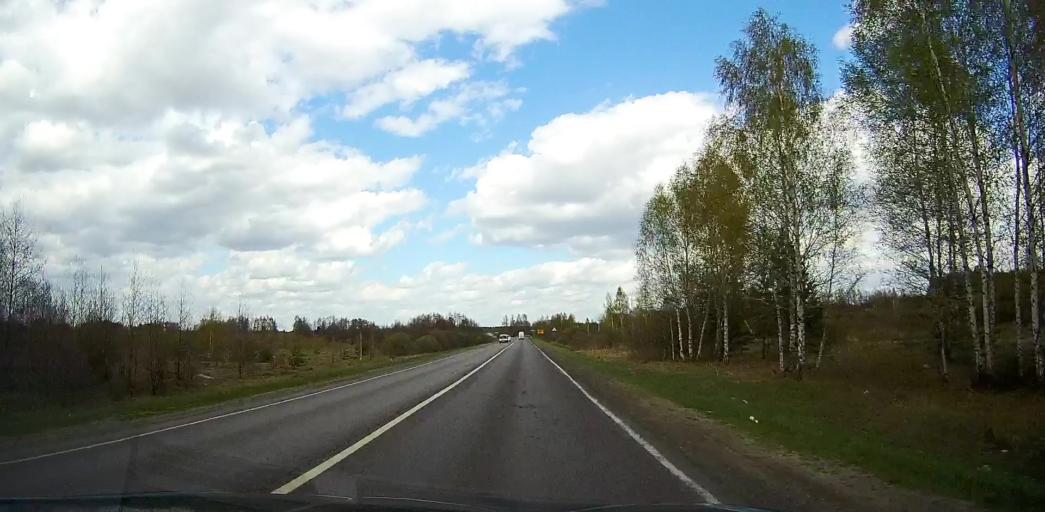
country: RU
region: Moskovskaya
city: Davydovo
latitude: 55.6307
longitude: 38.8652
